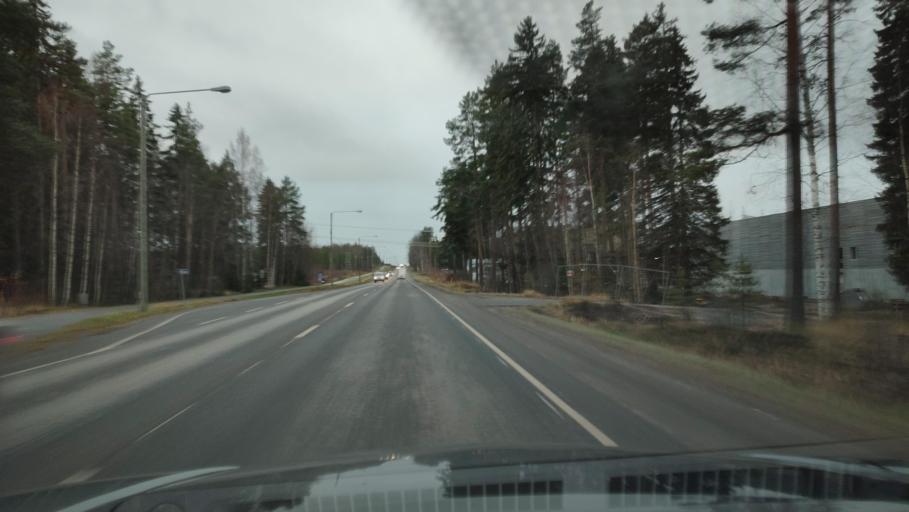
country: FI
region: Southern Ostrobothnia
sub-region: Seinaejoki
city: Seinaejoki
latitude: 62.7851
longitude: 22.7150
